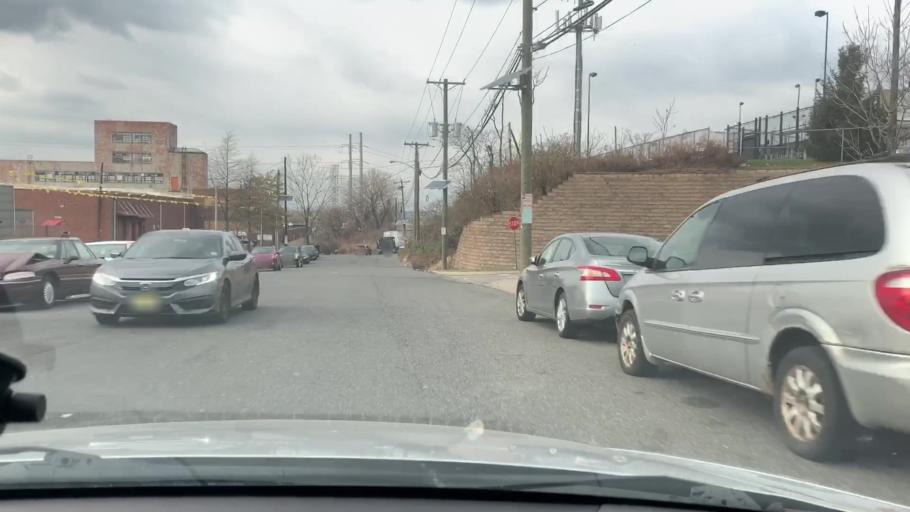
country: US
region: New Jersey
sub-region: Hudson County
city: North Bergen
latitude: 40.8032
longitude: -74.0205
